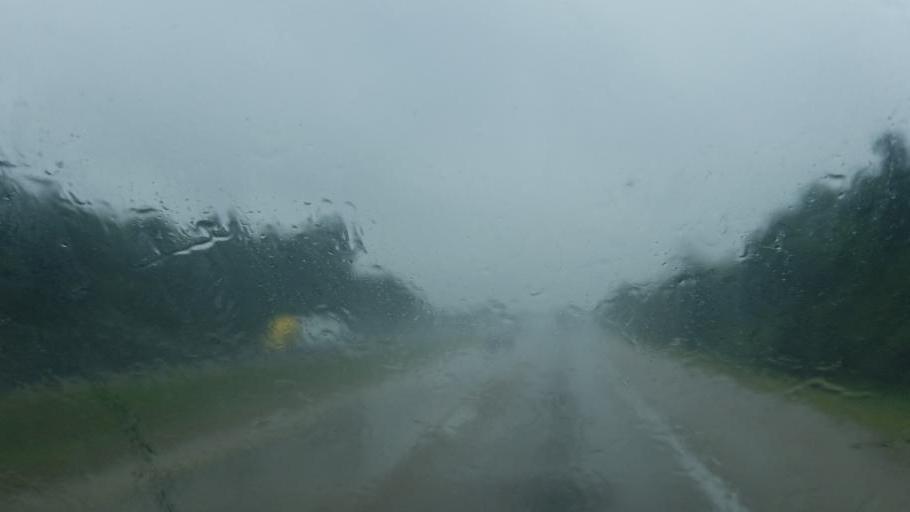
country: US
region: Indiana
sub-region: Delaware County
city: Yorktown
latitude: 40.2562
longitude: -85.5577
